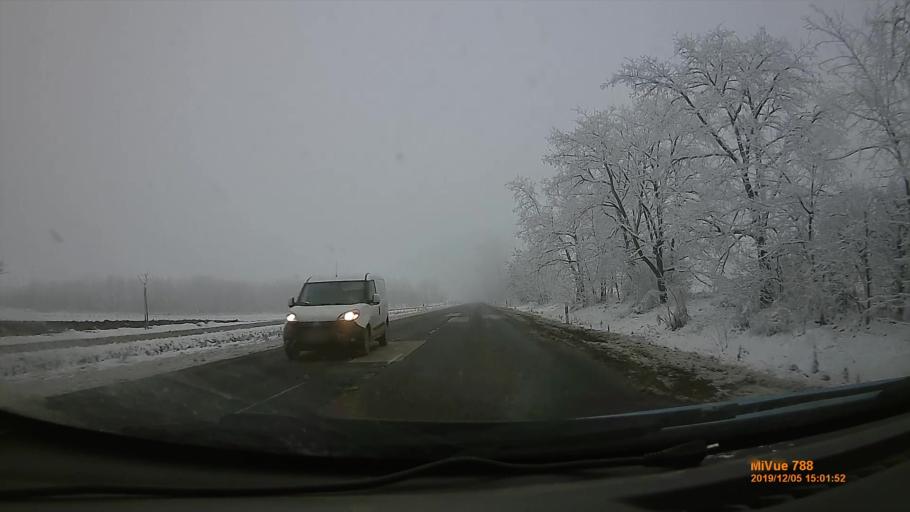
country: HU
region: Szabolcs-Szatmar-Bereg
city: Tiszanagyfalu
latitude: 48.0709
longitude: 21.5222
